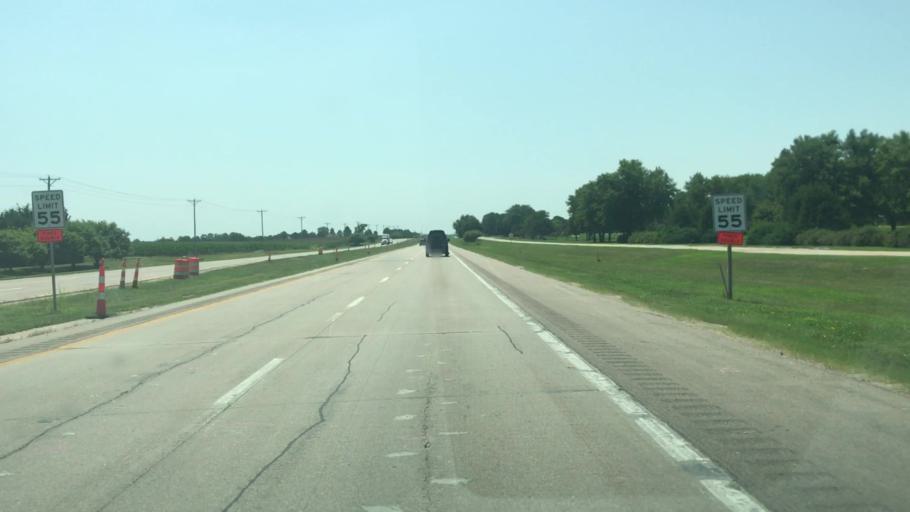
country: US
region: Nebraska
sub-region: Adams County
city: Hastings
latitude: 40.6404
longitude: -98.3820
